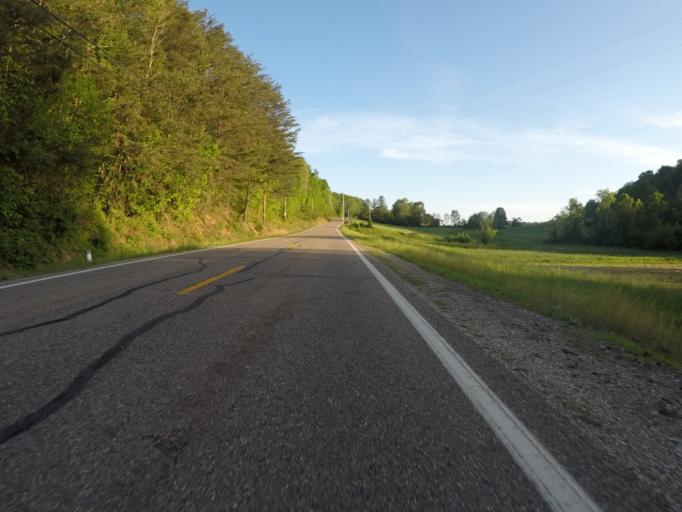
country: US
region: West Virginia
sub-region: Cabell County
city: Huntington
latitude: 38.5524
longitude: -82.4629
